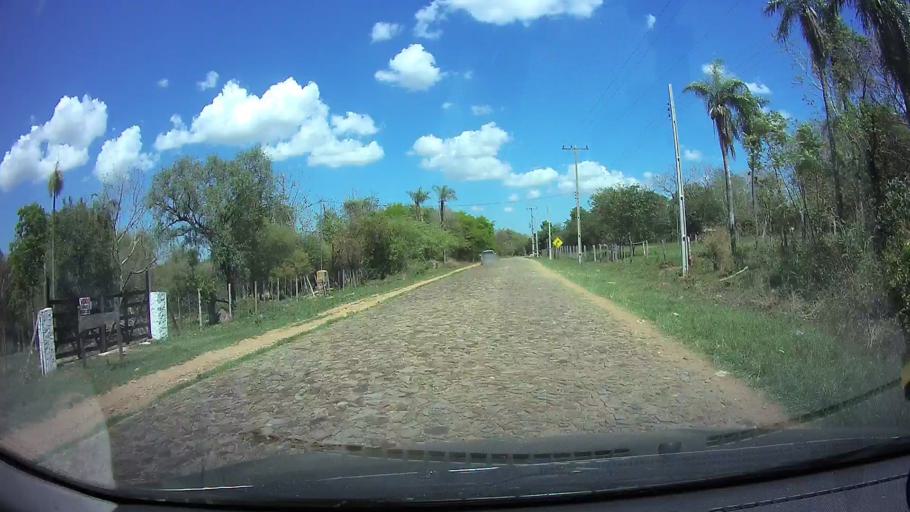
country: PY
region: Cordillera
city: Emboscada
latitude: -25.1168
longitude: -57.3058
